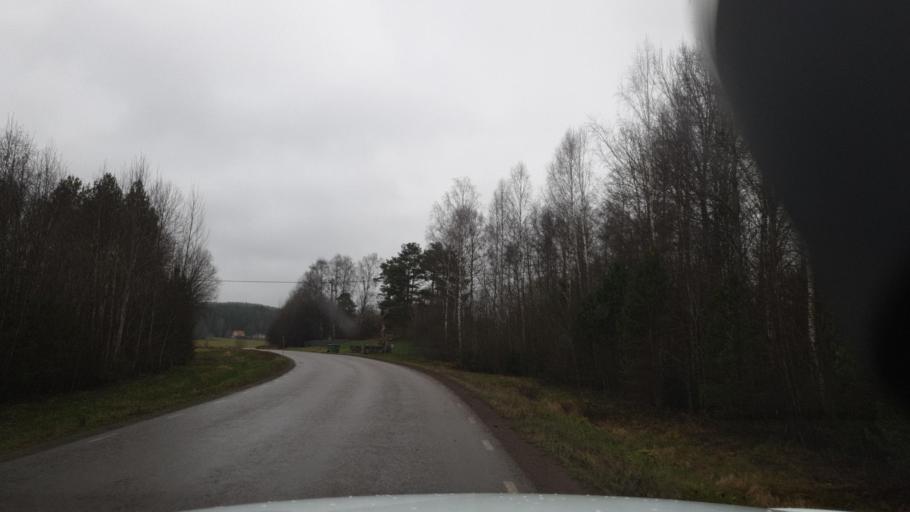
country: SE
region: Vaermland
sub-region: Eda Kommun
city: Charlottenberg
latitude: 59.7960
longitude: 12.2191
